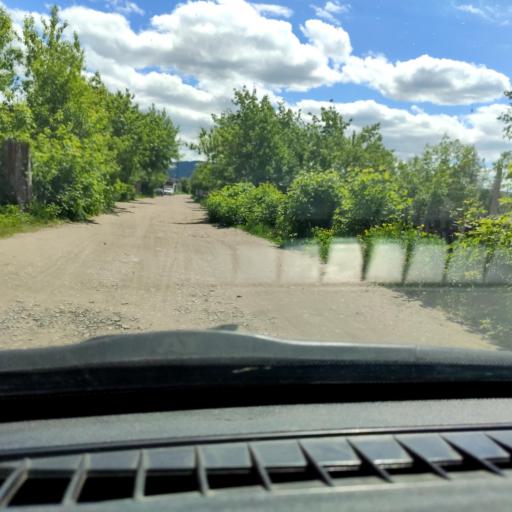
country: RU
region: Samara
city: Zhigulevsk
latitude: 53.4685
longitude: 49.5835
